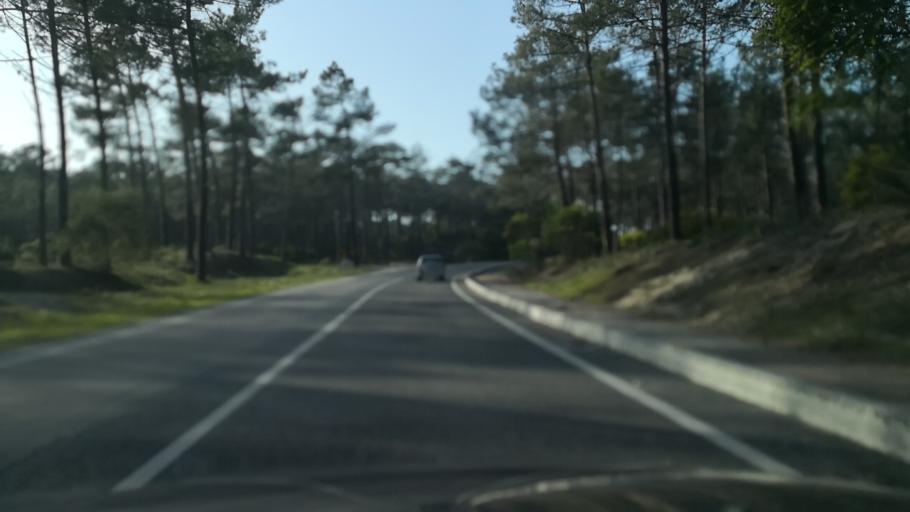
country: PT
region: Leiria
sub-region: Alcobaca
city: Pataias
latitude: 39.7525
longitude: -9.0213
